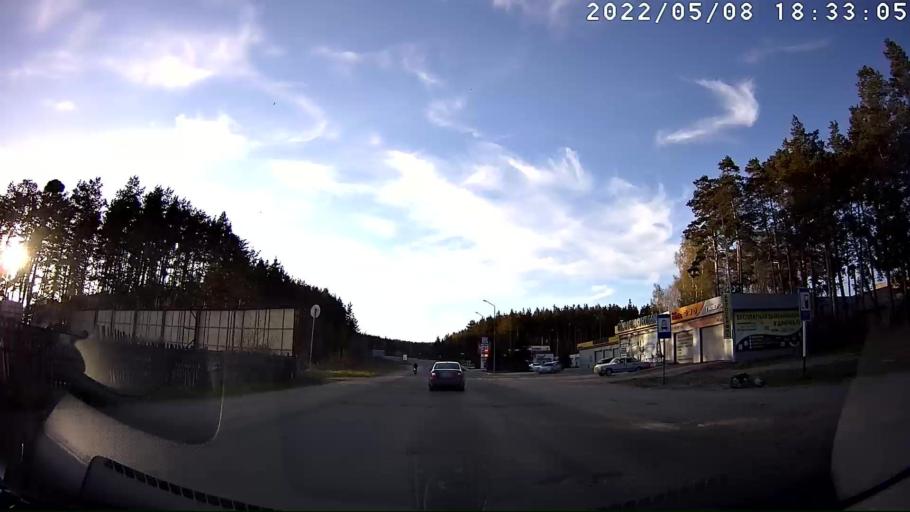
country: RU
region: Mariy-El
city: Volzhsk
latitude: 55.8882
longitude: 48.3589
